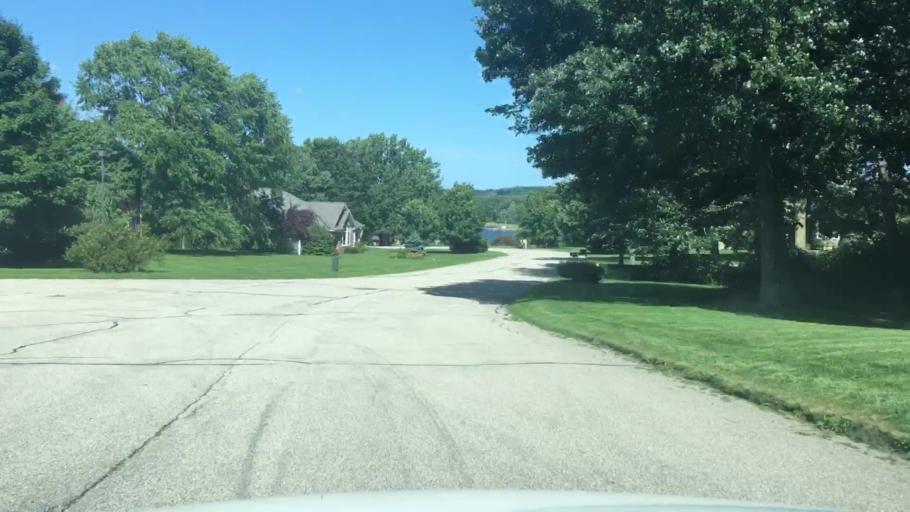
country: US
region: Maine
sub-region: York County
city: Eliot
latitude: 43.1694
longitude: -70.8336
